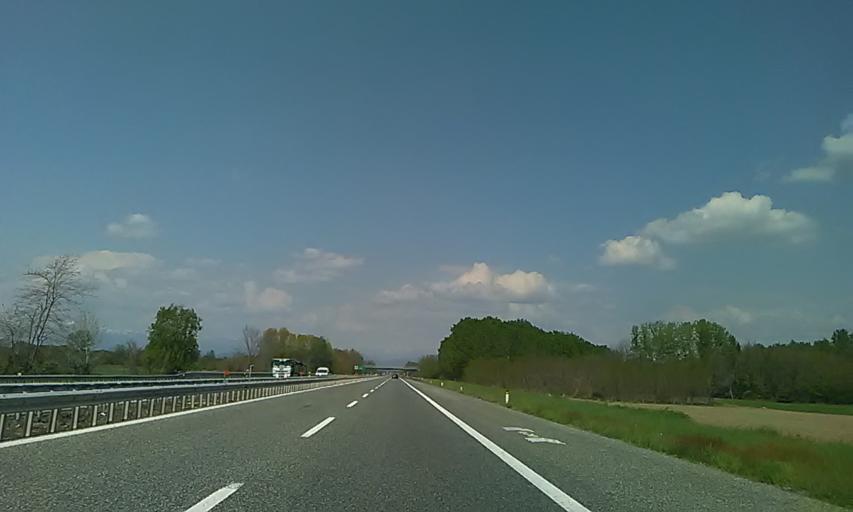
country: IT
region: Piedmont
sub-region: Provincia di Novara
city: Carpignano Sesia
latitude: 45.5466
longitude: 8.4249
